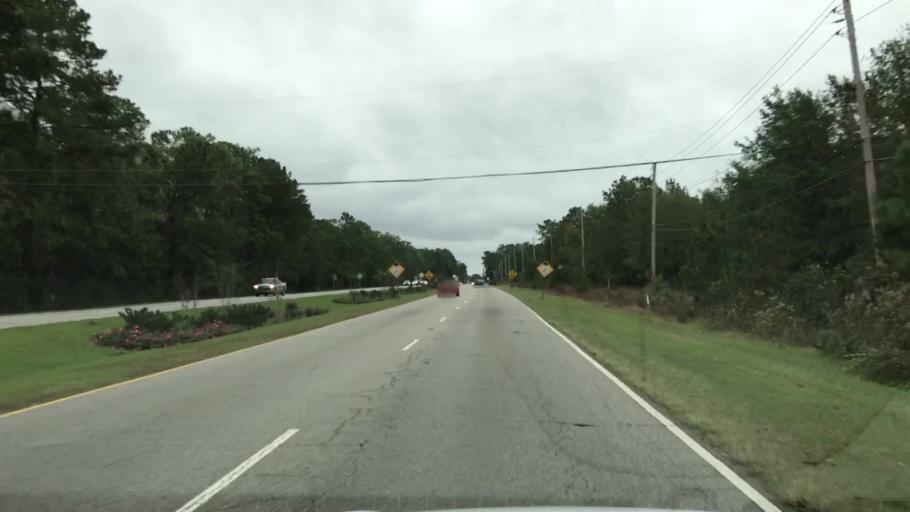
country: US
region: South Carolina
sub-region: Georgetown County
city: Georgetown
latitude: 33.3343
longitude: -79.3085
